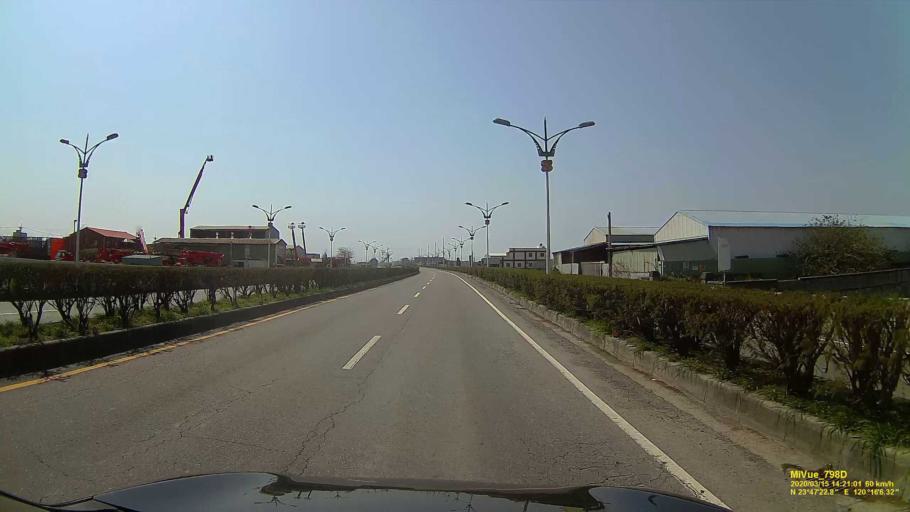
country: TW
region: Taiwan
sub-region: Yunlin
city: Douliu
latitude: 23.7897
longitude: 120.2681
